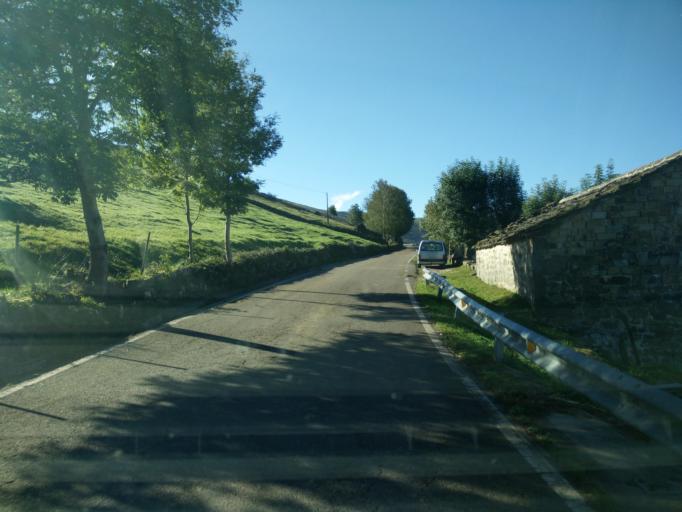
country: ES
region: Cantabria
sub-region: Provincia de Cantabria
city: San Pedro del Romeral
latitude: 43.1004
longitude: -3.8193
